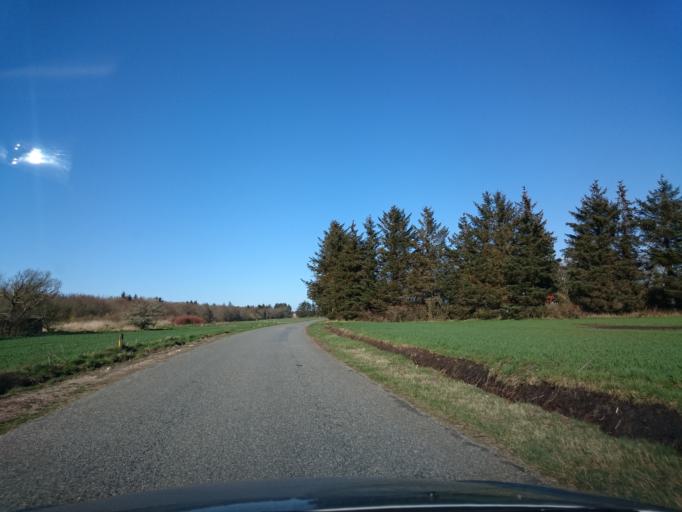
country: DK
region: North Denmark
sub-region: Hjorring Kommune
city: Hirtshals
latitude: 57.5607
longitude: 10.0728
